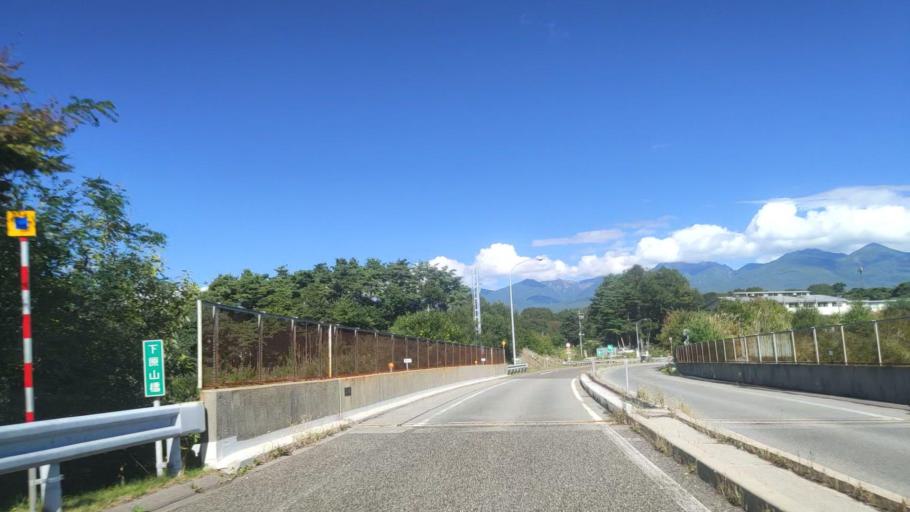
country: JP
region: Nagano
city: Chino
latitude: 35.9380
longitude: 138.2111
